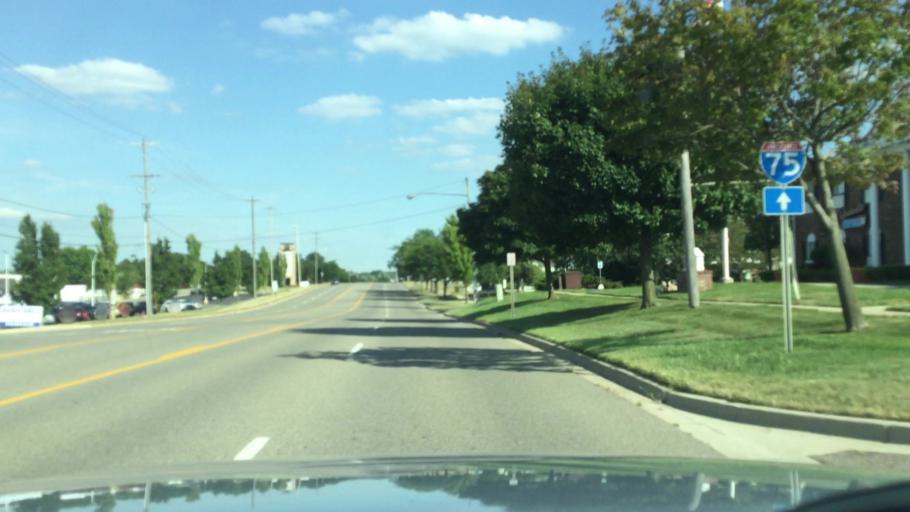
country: US
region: Michigan
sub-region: Genesee County
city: Grand Blanc
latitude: 42.9192
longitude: -83.6194
